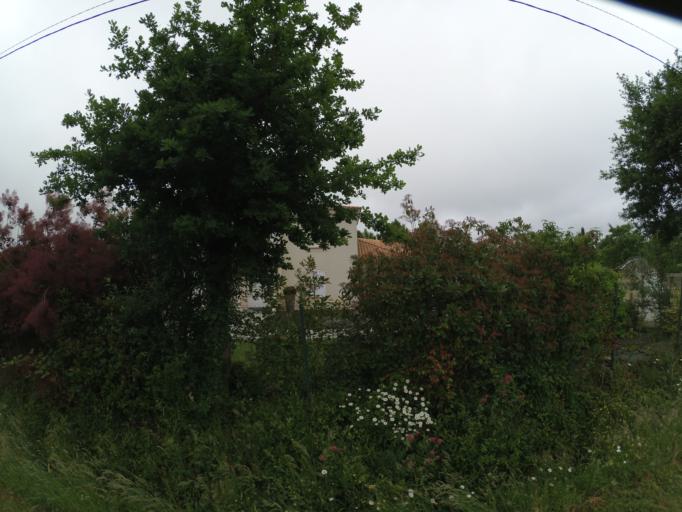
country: FR
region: Pays de la Loire
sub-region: Departement de la Vendee
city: La Roche-sur-Yon
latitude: 46.6429
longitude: -1.4334
